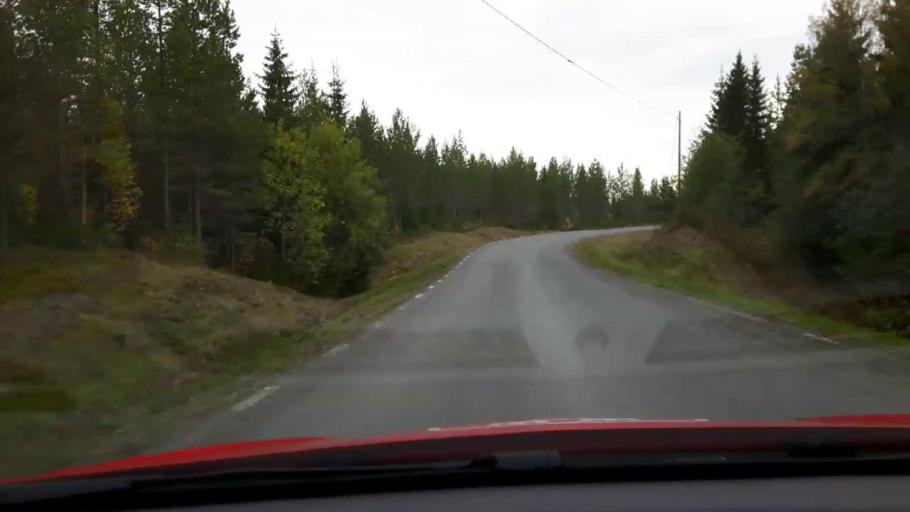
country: SE
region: Jaemtland
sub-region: Krokoms Kommun
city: Krokom
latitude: 63.2100
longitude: 14.1175
